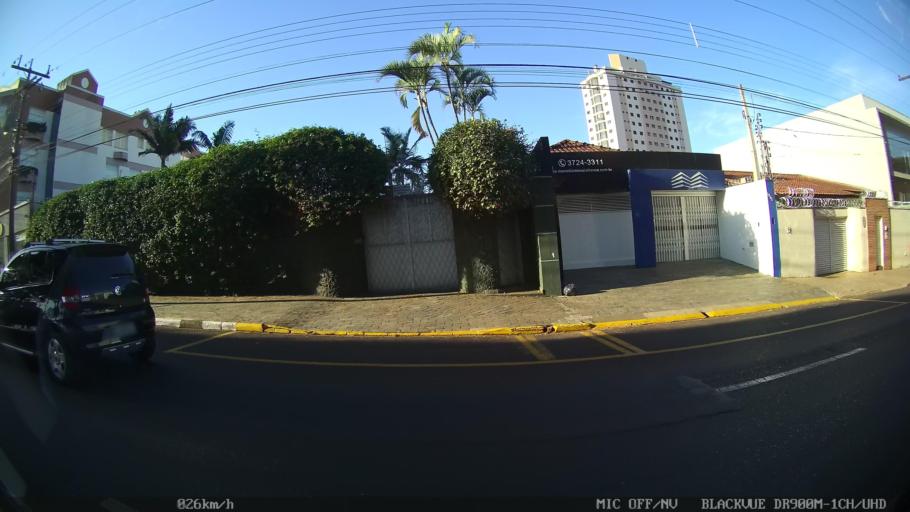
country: BR
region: Sao Paulo
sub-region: Franca
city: Franca
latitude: -20.5347
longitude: -47.3940
